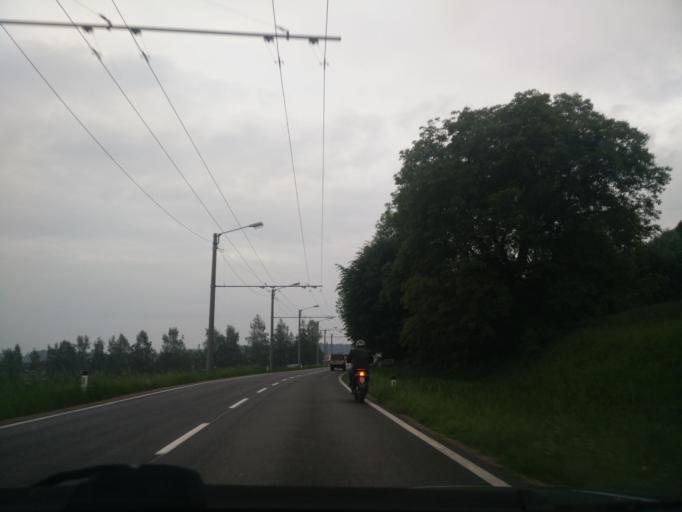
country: AT
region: Salzburg
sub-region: Politischer Bezirk Salzburg-Umgebung
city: Hallwang
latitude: 47.8277
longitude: 13.0818
